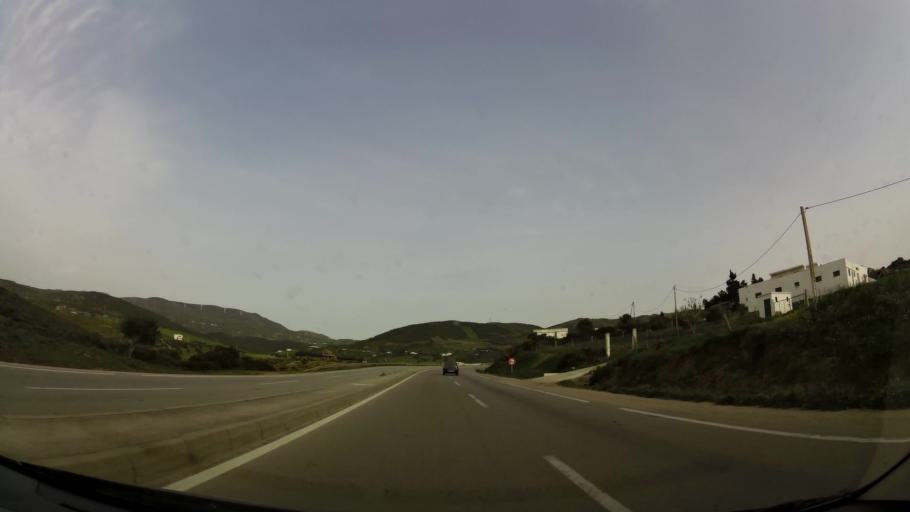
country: MA
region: Tanger-Tetouan
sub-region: Tanger-Assilah
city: Dar Chaoui
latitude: 35.5674
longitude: -5.6092
